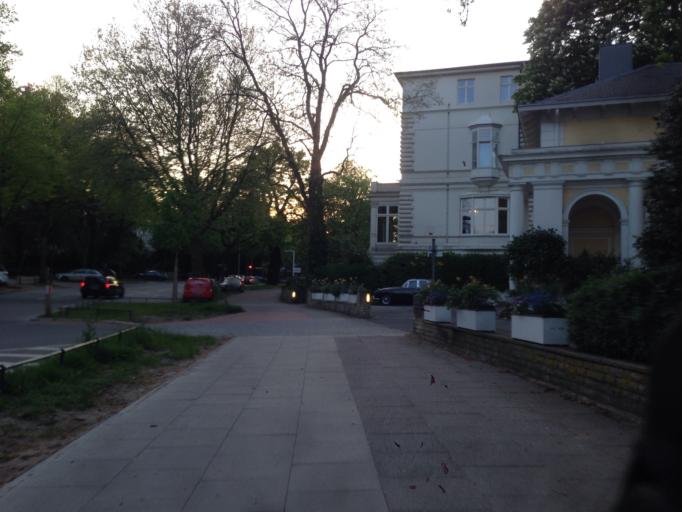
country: DE
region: Hamburg
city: Hamburg
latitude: 53.5779
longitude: 9.9990
